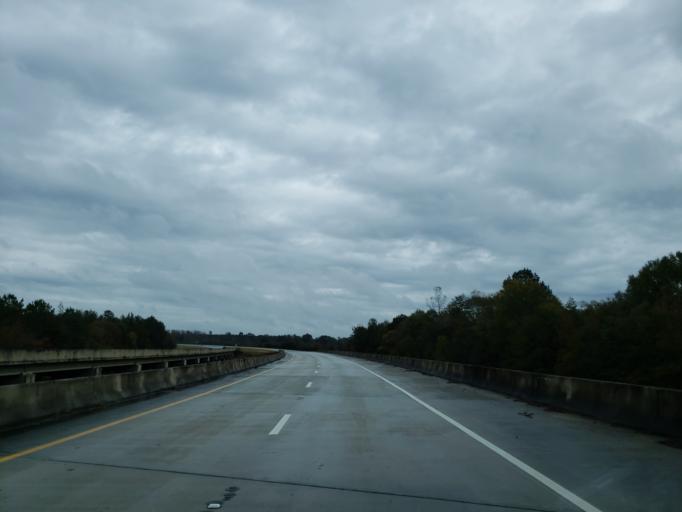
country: US
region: Mississippi
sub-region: Wayne County
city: Waynesboro
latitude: 31.6826
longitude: -88.6793
